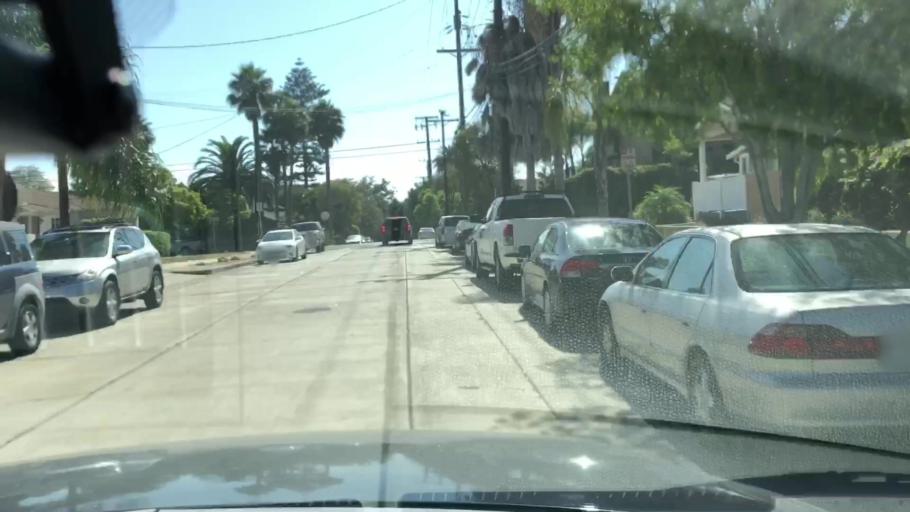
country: US
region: California
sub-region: Santa Barbara County
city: Mission Canyon
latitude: 34.4311
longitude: -119.7190
